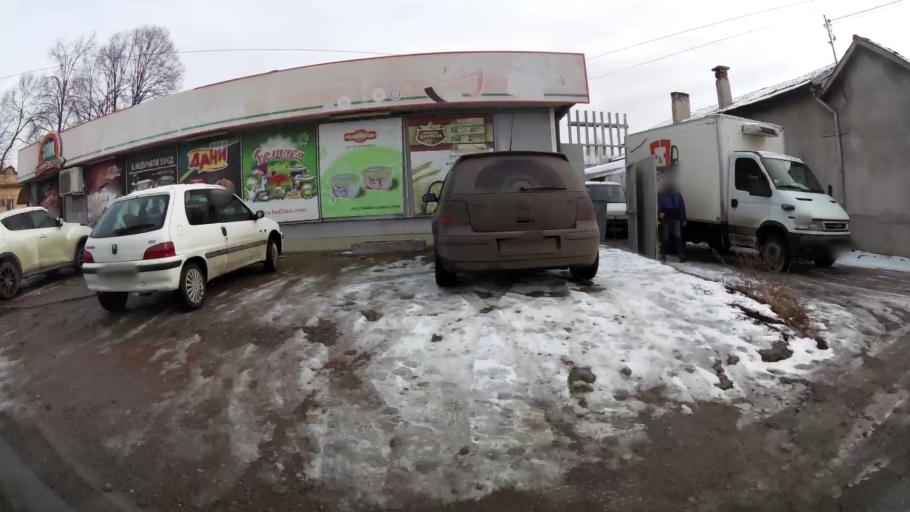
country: BG
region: Sofia-Capital
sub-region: Stolichna Obshtina
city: Sofia
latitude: 42.7121
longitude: 23.4117
